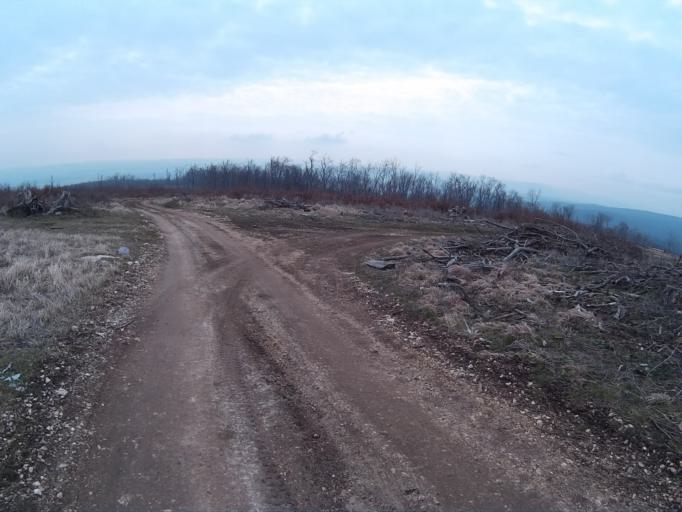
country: HU
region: Veszprem
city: Zirc
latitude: 47.1777
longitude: 17.8516
